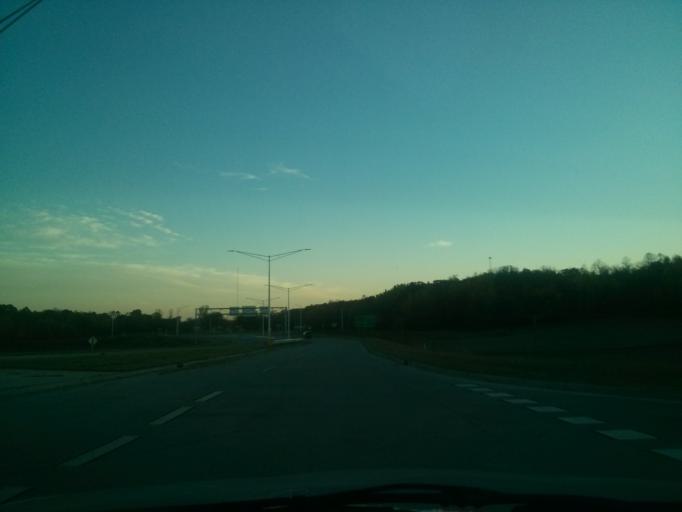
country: US
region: Wisconsin
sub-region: Pierce County
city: River Falls
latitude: 44.8978
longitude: -92.6494
